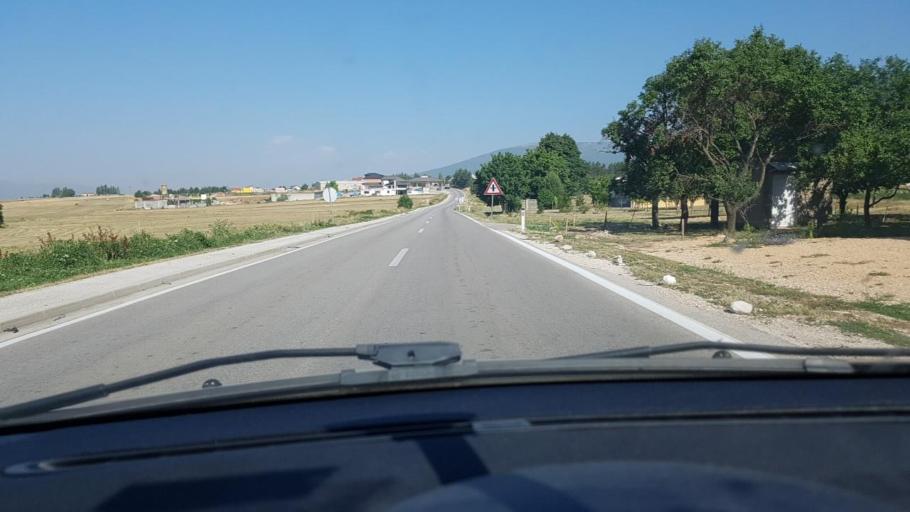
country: BA
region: Federation of Bosnia and Herzegovina
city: Livno
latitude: 43.8407
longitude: 16.9724
